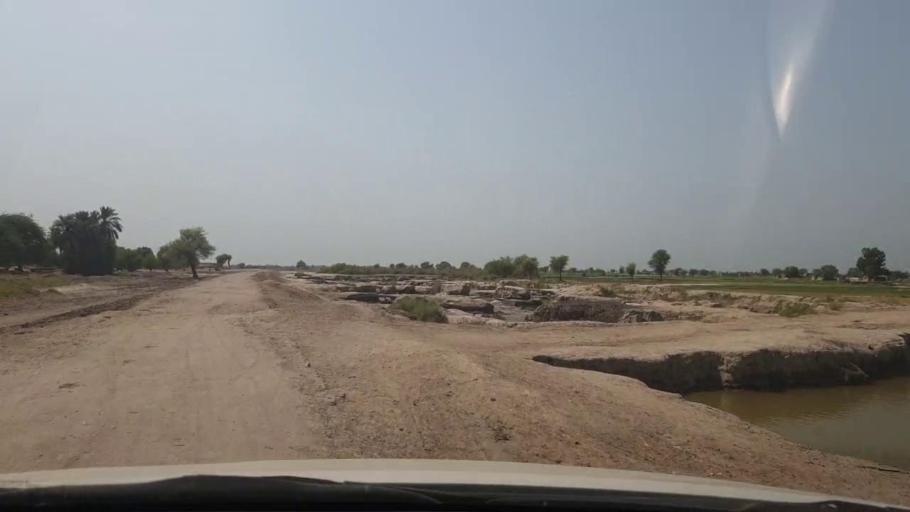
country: PK
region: Sindh
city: Shikarpur
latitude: 28.0071
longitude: 68.7118
